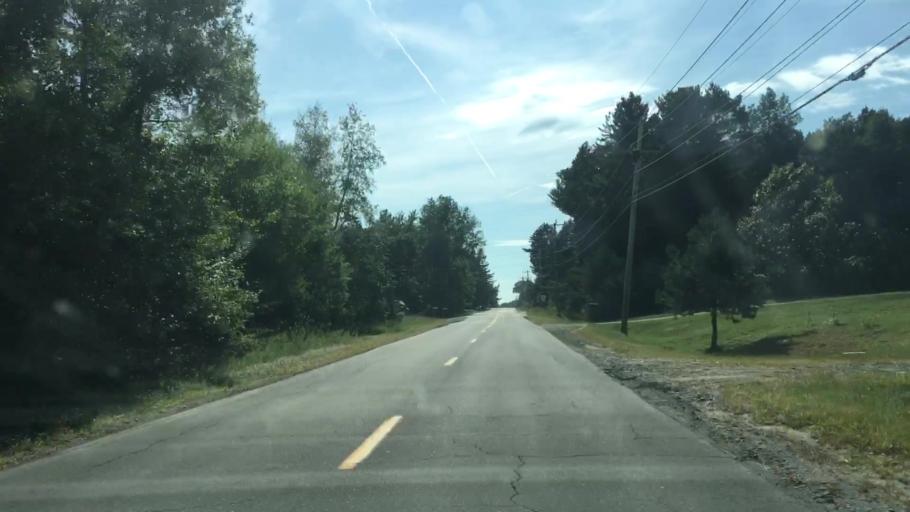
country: US
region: Maine
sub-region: Penobscot County
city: Lincoln
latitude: 45.4313
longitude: -68.4692
